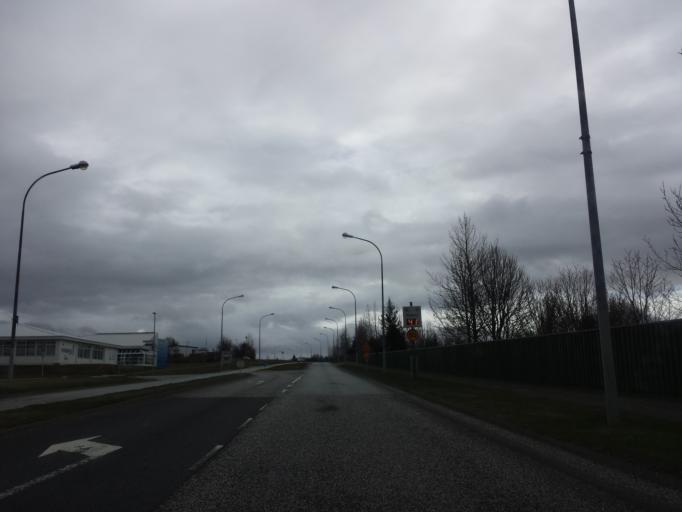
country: IS
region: Capital Region
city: Gardabaer
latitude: 64.0871
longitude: -21.9180
